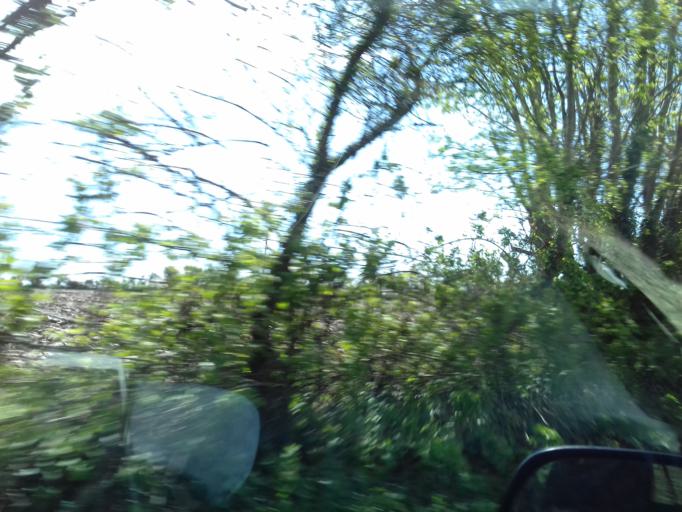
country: IE
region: Munster
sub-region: Waterford
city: Dunmore East
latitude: 52.2233
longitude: -6.8616
